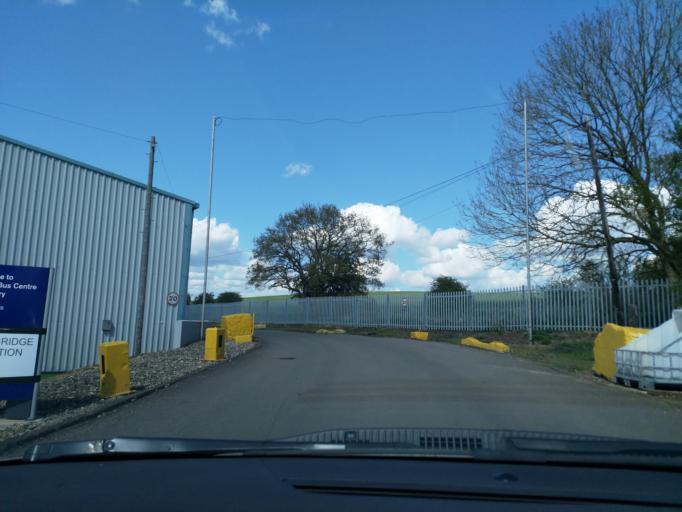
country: GB
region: England
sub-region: Oxfordshire
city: Adderbury
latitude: 52.0337
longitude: -1.2917
